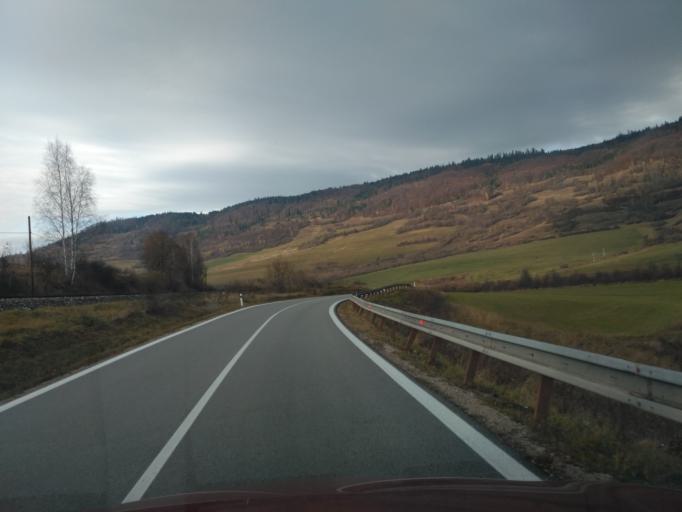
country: SK
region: Kosicky
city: Spisska Nova Ves
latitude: 48.8333
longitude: 20.6464
